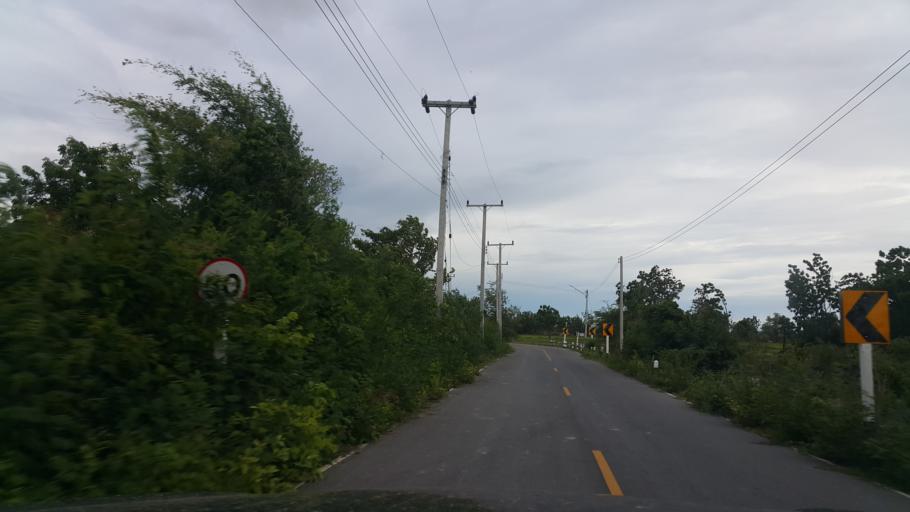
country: TH
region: Sukhothai
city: Ban Dan Lan Hoi
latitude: 17.1605
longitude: 99.5016
